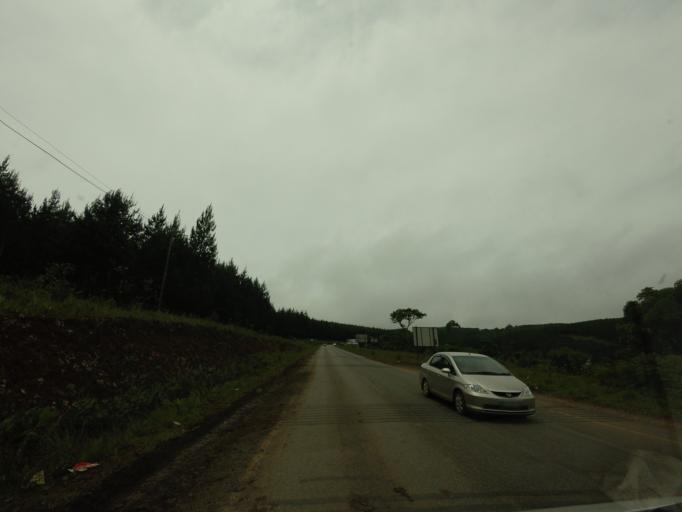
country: SZ
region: Hhohho
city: Piggs Peak
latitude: -25.9845
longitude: 31.2403
